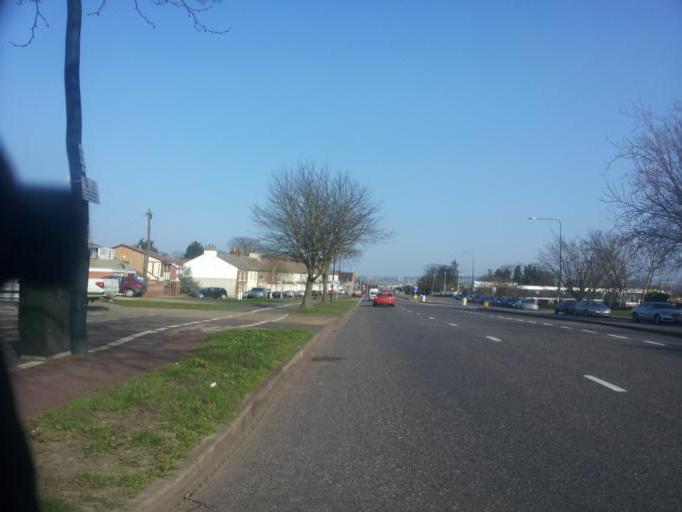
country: GB
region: England
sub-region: Kent
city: Strood
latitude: 51.3970
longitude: 0.4814
